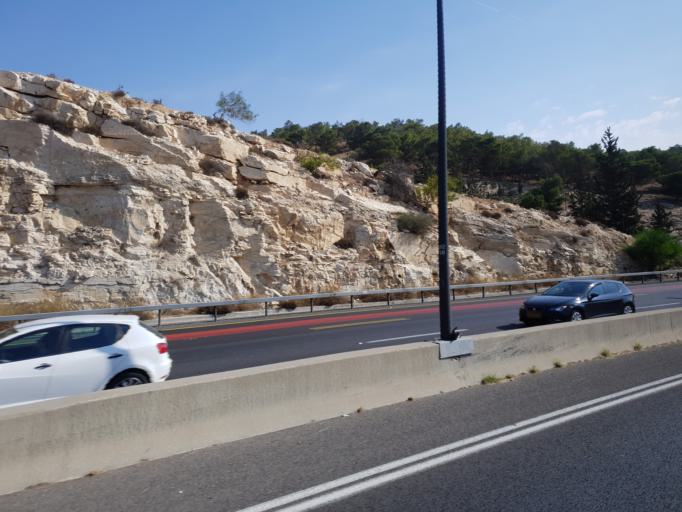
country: PS
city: Az Za`ayyim
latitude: 31.7881
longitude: 35.2787
